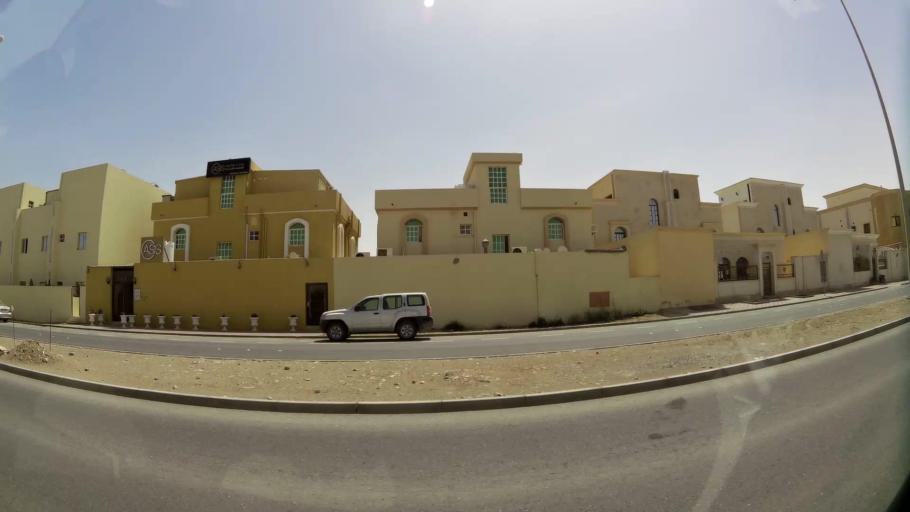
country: QA
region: Baladiyat Umm Salal
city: Umm Salal Muhammad
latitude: 25.3661
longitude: 51.4283
